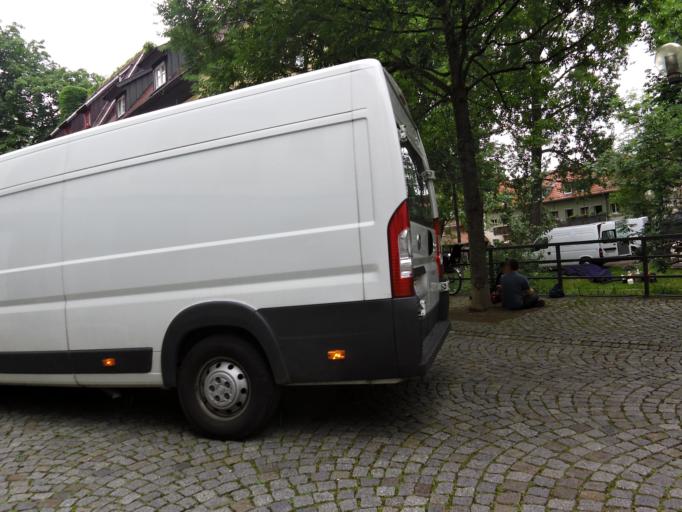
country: DE
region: Thuringia
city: Erfurt
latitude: 50.9795
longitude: 11.0299
